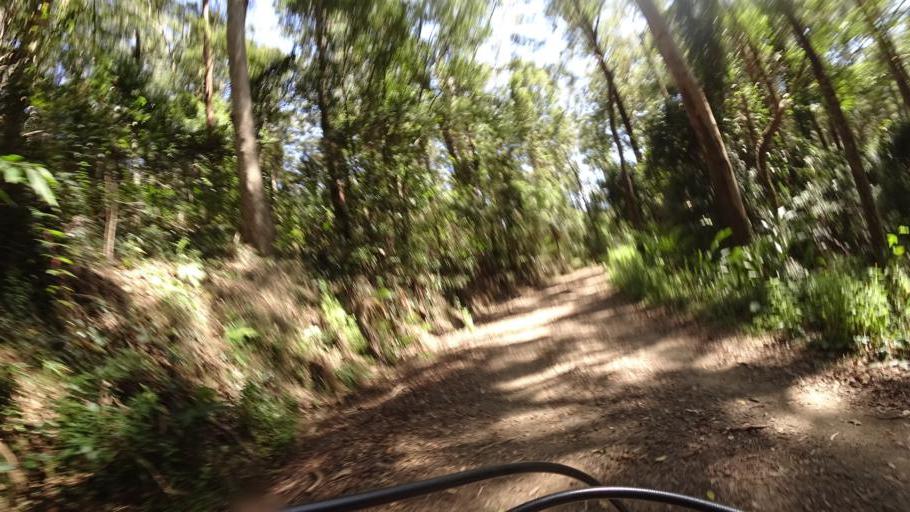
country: AU
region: Queensland
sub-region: Moreton Bay
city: Highvale
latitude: -27.4048
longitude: 152.7999
